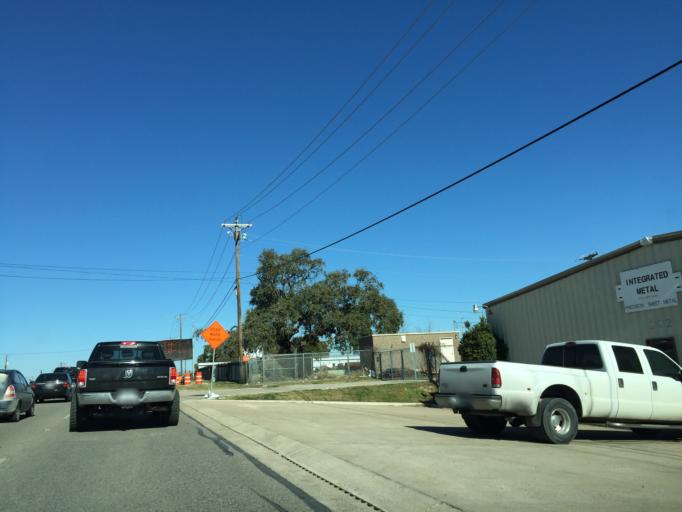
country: US
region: Texas
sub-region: Williamson County
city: Leander
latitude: 30.5745
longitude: -97.8711
